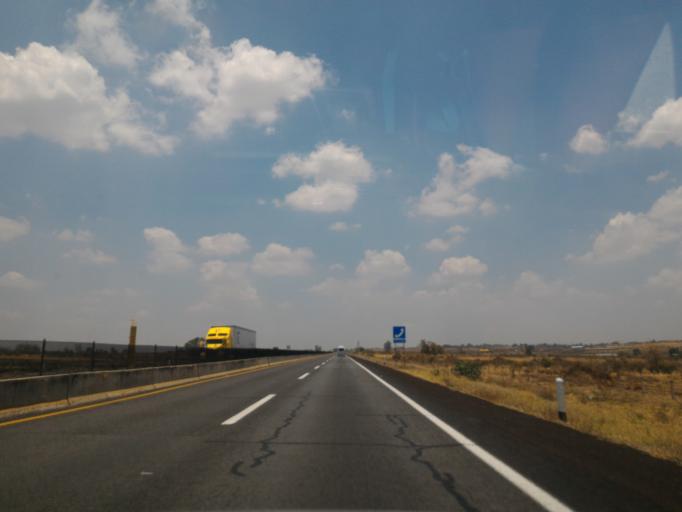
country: MX
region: Jalisco
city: Acatic
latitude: 20.7162
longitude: -102.9459
